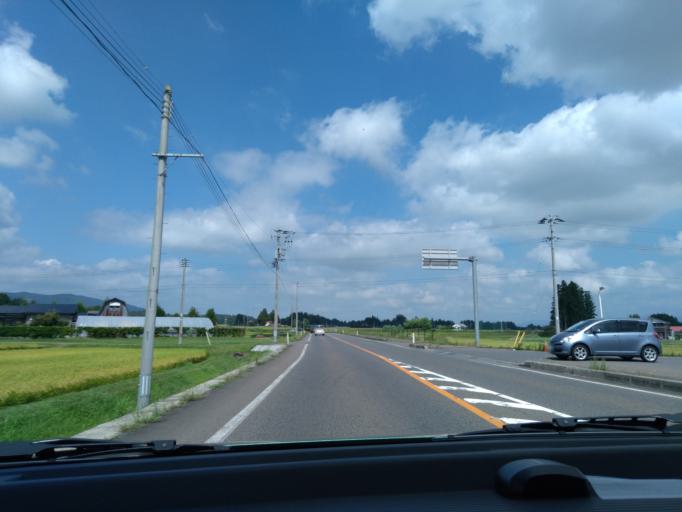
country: JP
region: Iwate
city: Hanamaki
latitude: 39.4611
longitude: 141.1014
